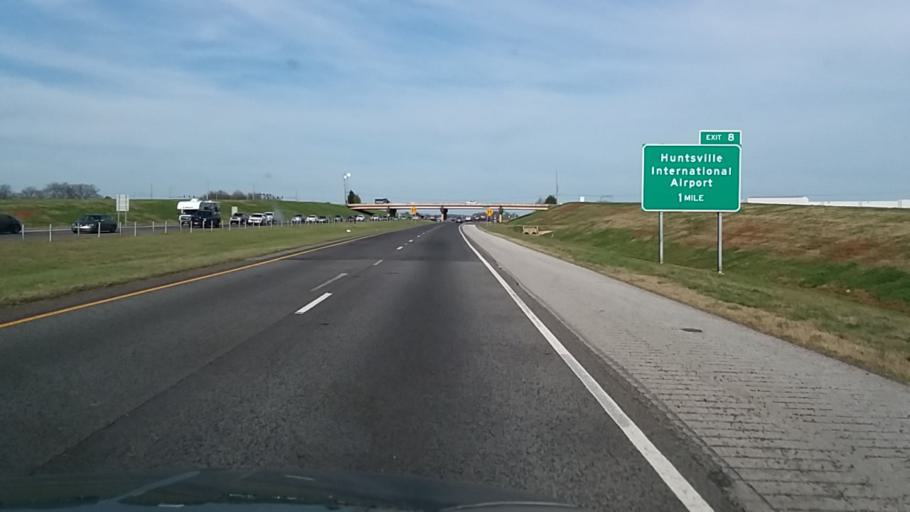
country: US
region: Alabama
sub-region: Madison County
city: Madison
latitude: 34.6599
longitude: -86.7905
